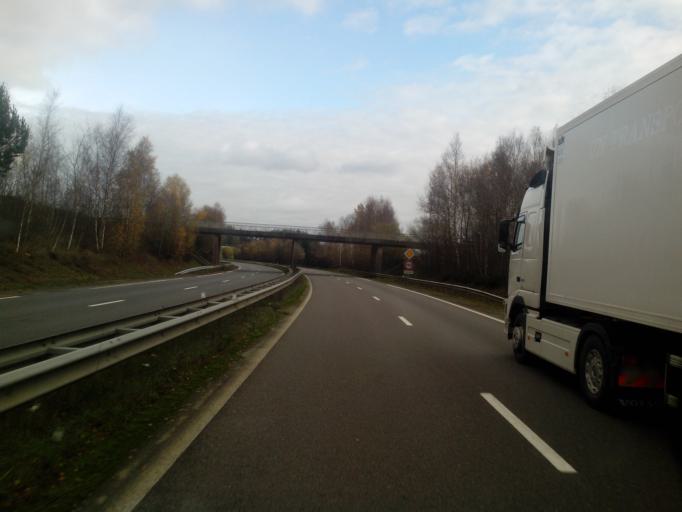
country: FR
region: Brittany
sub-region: Departement d'Ille-et-Vilaine
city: Saint-Meen-le-Grand
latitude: 48.1779
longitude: -2.1942
